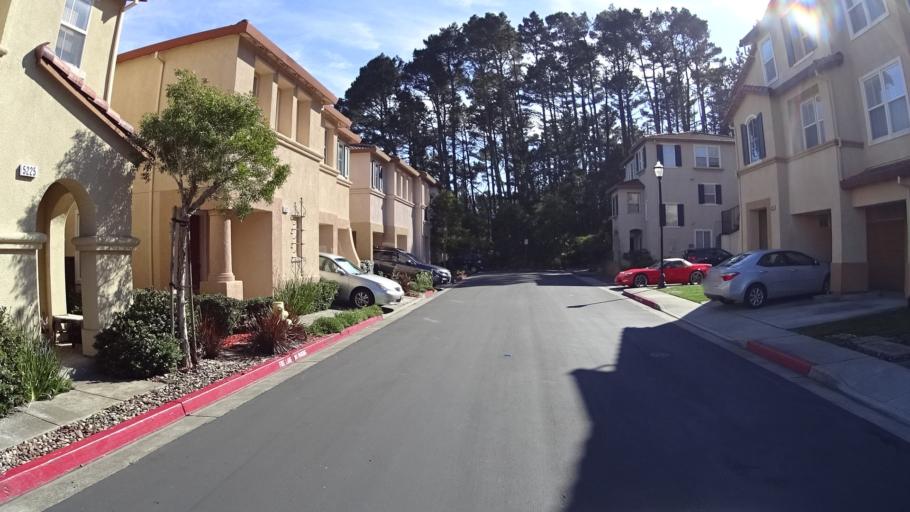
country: US
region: California
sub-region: San Mateo County
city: Pacifica
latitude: 37.6401
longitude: -122.4621
